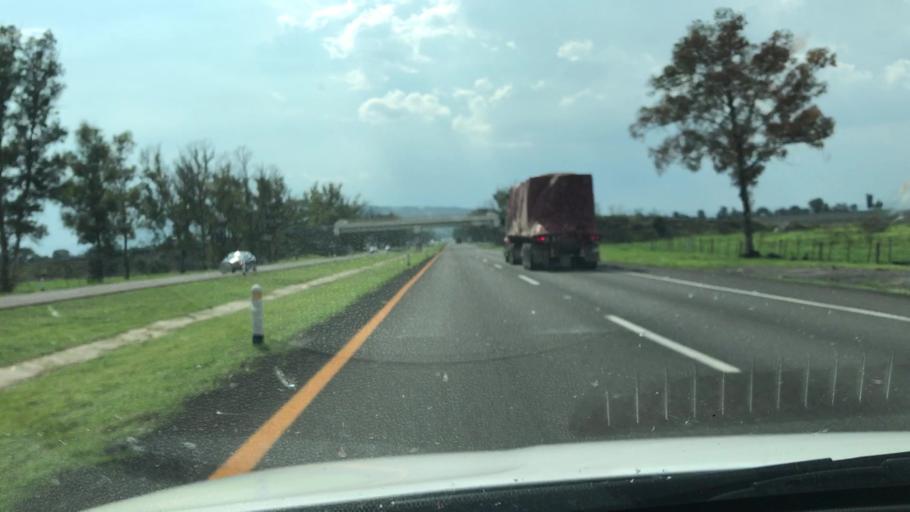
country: MX
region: Jalisco
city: Ocotlan
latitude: 20.3859
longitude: -102.7090
